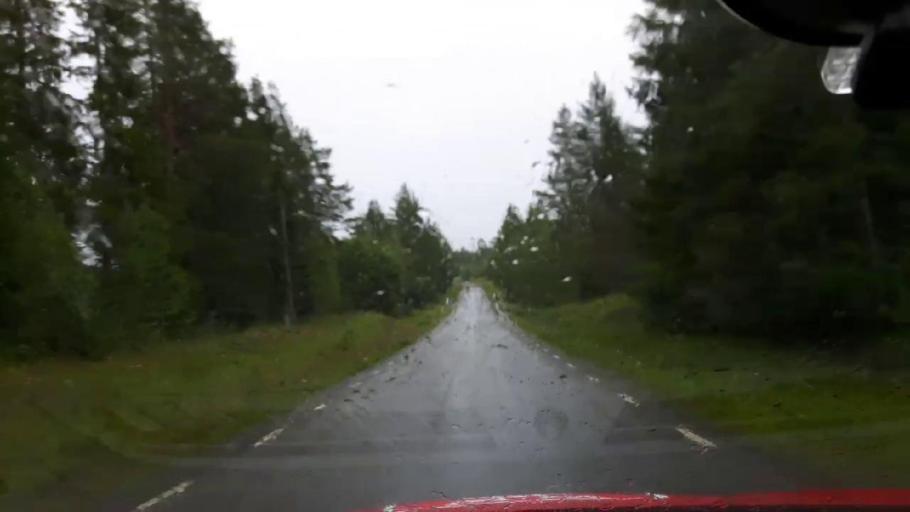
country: SE
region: Jaemtland
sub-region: OEstersunds Kommun
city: Brunflo
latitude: 62.9811
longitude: 14.8238
